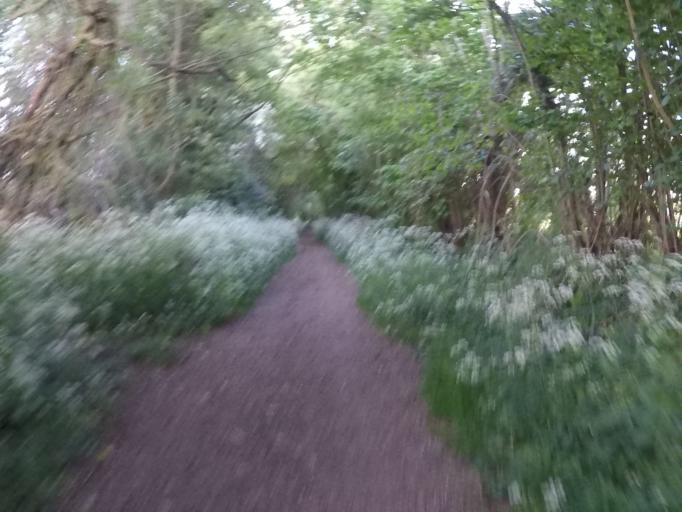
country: GB
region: England
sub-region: Oxfordshire
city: Witney
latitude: 51.8246
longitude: -1.4879
